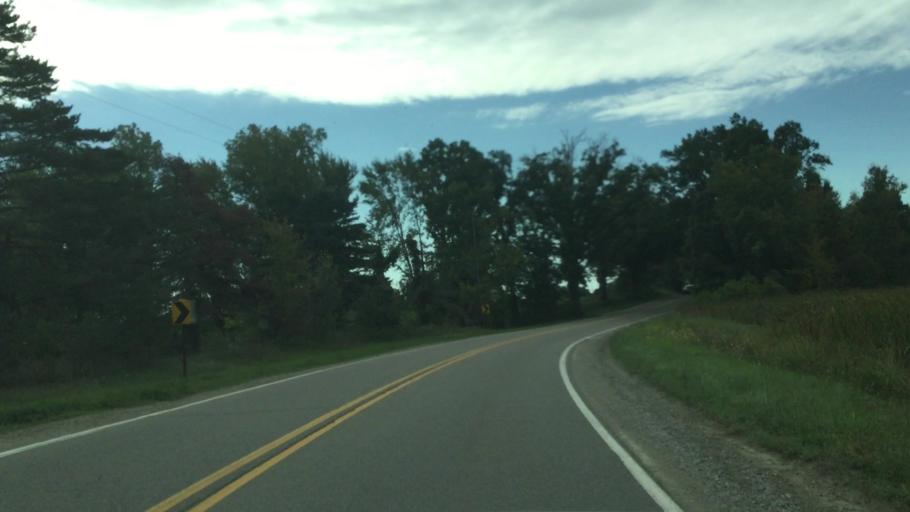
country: US
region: Michigan
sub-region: Genesee County
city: Argentine
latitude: 42.6950
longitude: -83.8383
